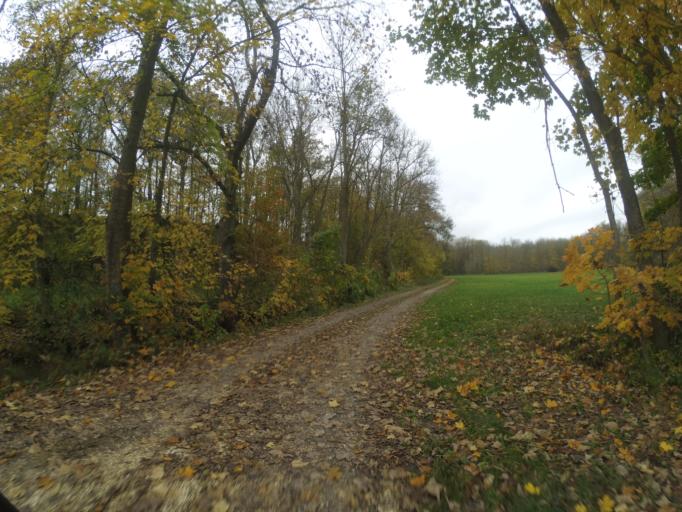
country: DE
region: Baden-Wuerttemberg
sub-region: Tuebingen Region
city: Staig
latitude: 48.3439
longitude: 10.0030
